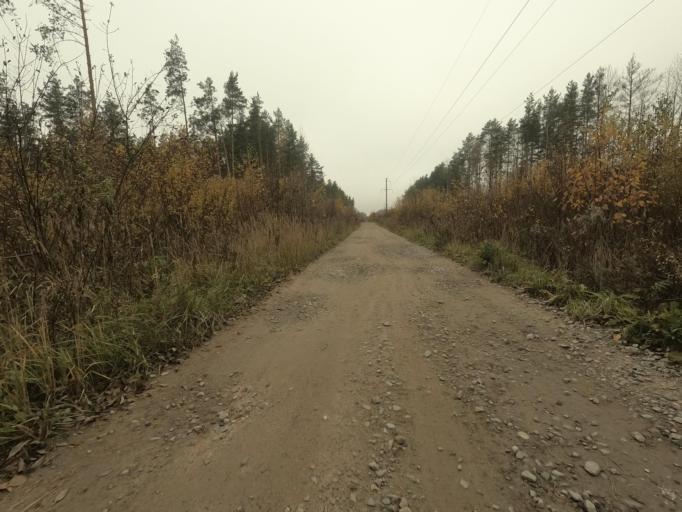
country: RU
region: Leningrad
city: Pavlovo
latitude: 59.7679
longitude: 30.9361
